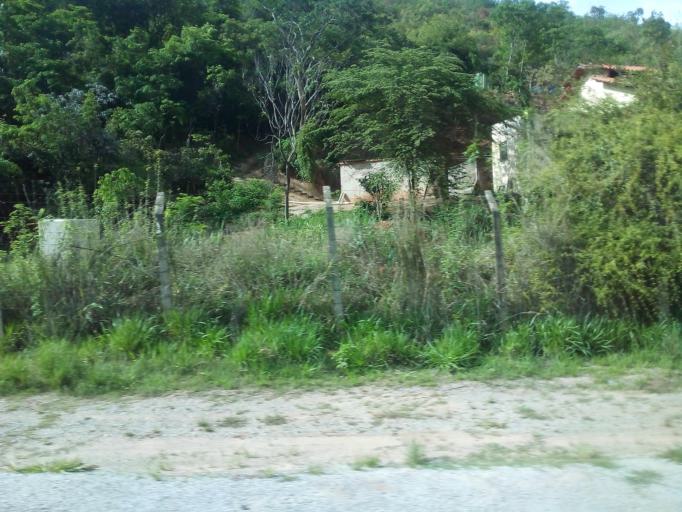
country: BR
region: Minas Gerais
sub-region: Raposos
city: Raposos
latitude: -19.8698
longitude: -43.8319
